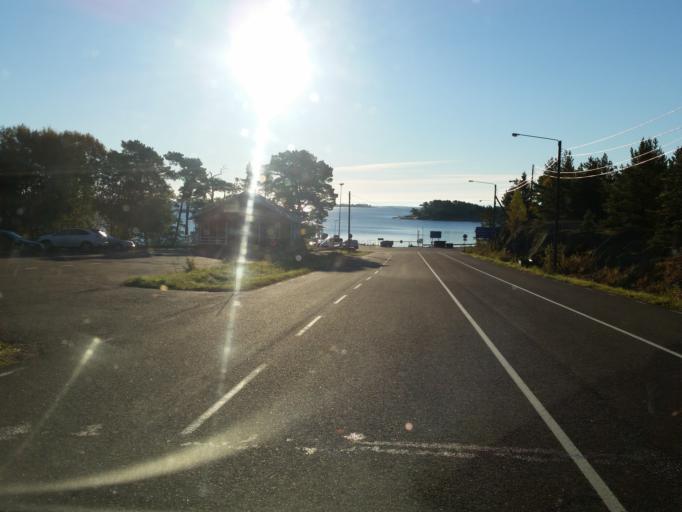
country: AX
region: Alands skaergard
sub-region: Vardoe
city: Vardoe
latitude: 60.2253
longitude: 20.4116
